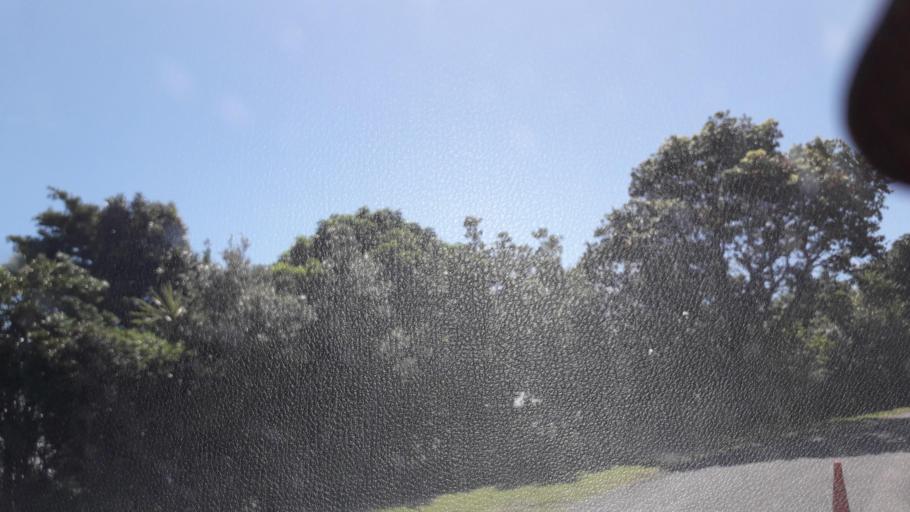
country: NZ
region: Northland
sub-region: Far North District
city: Paihia
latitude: -35.2245
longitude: 174.2597
